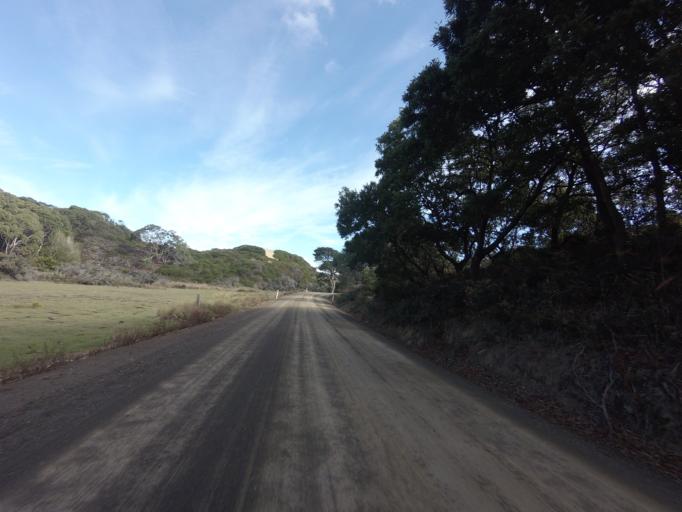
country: AU
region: Tasmania
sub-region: Clarence
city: Sandford
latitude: -43.0840
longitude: 147.6798
